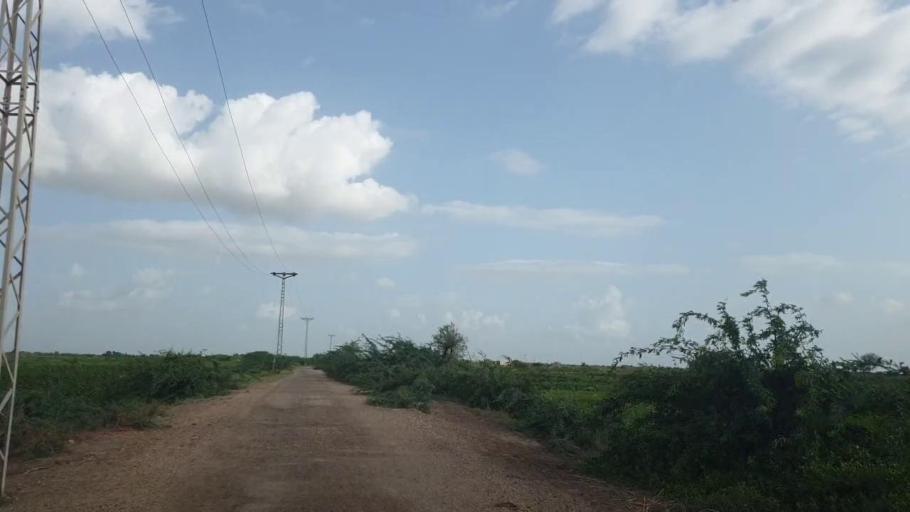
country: PK
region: Sindh
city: Kadhan
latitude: 24.6384
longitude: 69.0806
